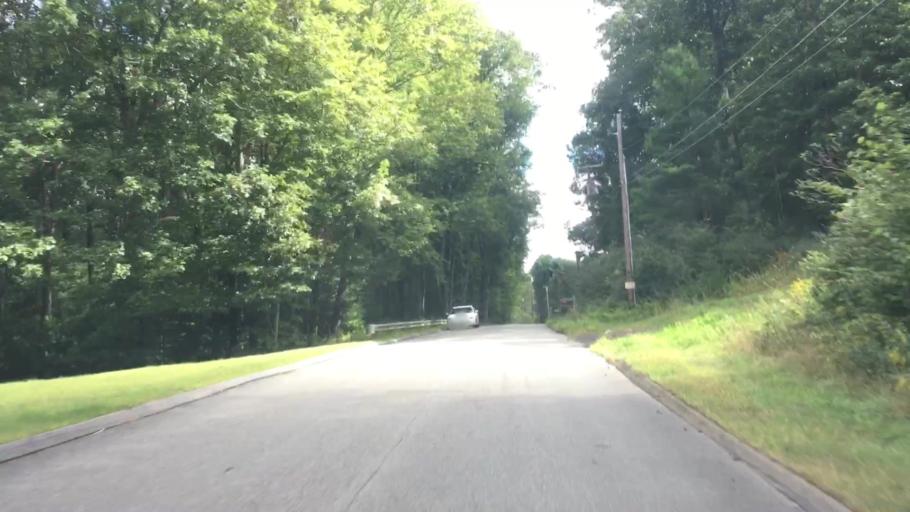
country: US
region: Connecticut
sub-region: Tolland County
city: Stafford Springs
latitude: 41.9176
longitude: -72.2216
